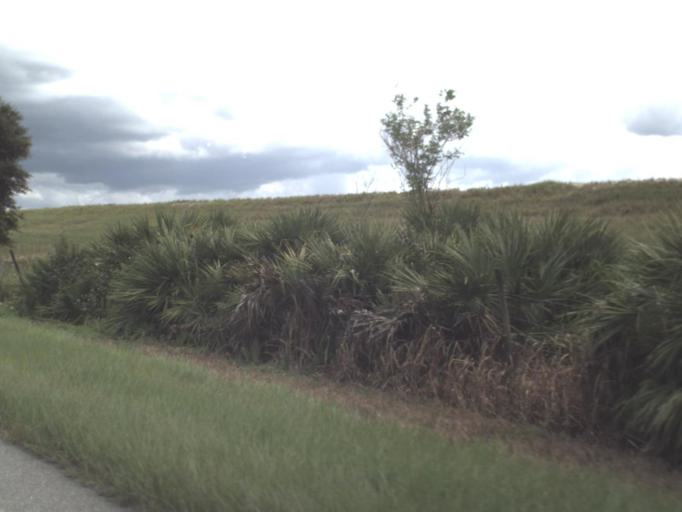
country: US
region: Florida
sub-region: Hillsborough County
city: Balm
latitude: 27.6394
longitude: -82.0626
